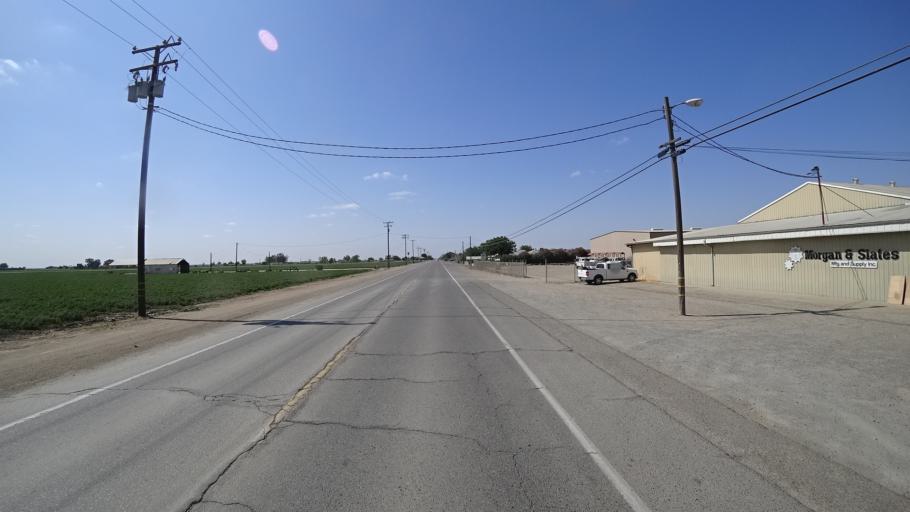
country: US
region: California
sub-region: Kings County
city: Home Garden
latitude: 36.2897
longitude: -119.6370
